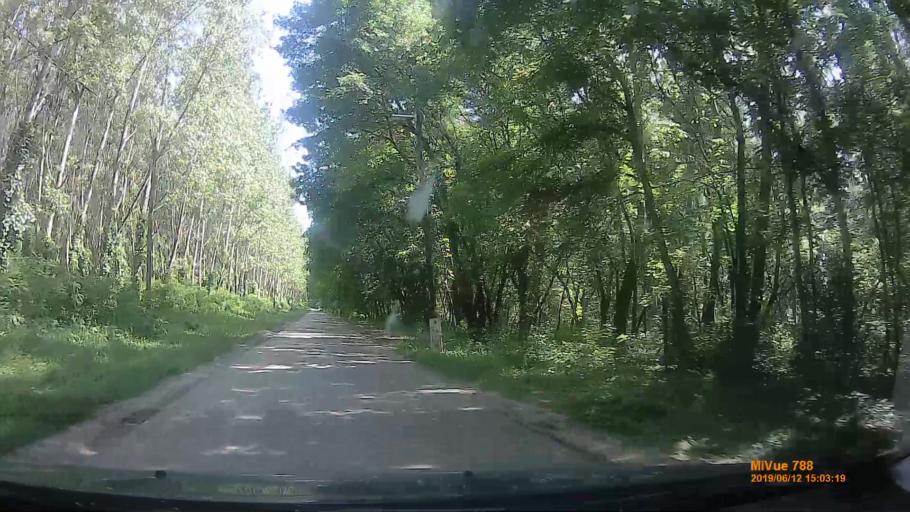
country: HU
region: Csongrad
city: Mako
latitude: 46.2032
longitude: 20.4656
